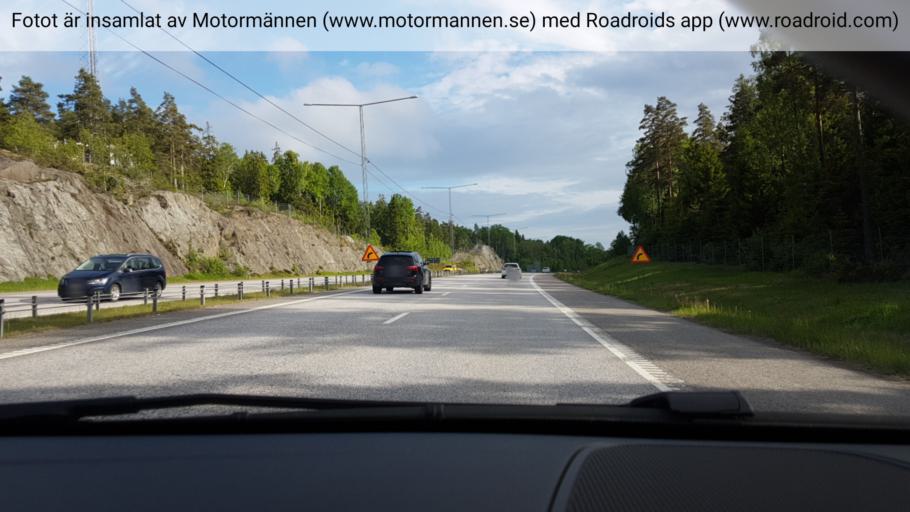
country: SE
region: Stockholm
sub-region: Haninge Kommun
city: Haninge
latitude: 59.1425
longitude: 18.1609
